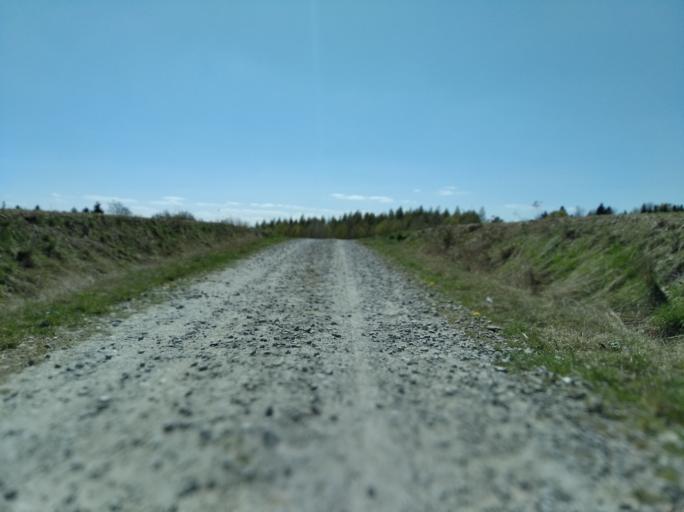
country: PL
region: Subcarpathian Voivodeship
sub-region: Powiat strzyzowski
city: Wisniowa
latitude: 49.9042
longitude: 21.7111
